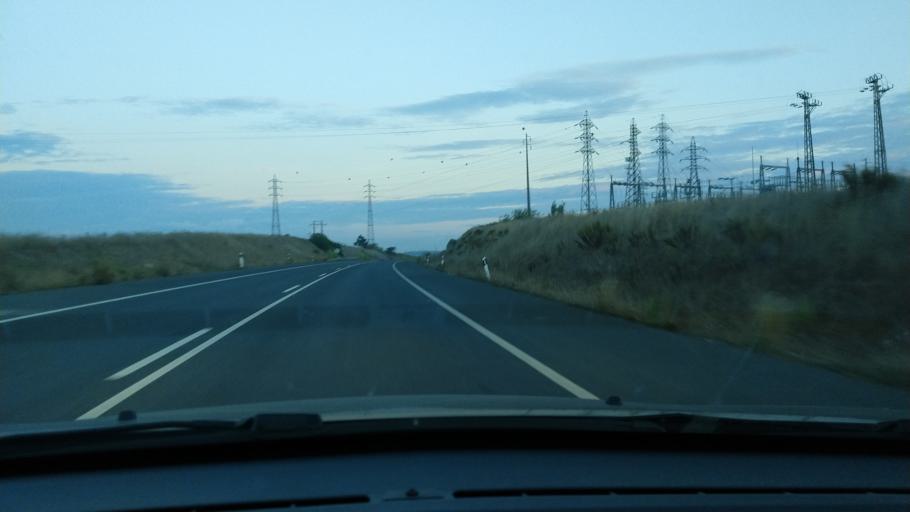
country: PT
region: Leiria
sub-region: Peniche
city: Atouguia da Baleia
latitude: 39.3282
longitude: -9.3198
